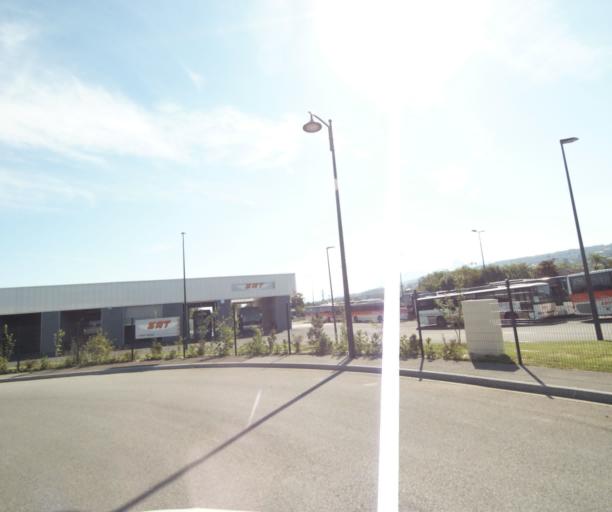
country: FR
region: Rhone-Alpes
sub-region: Departement de la Haute-Savoie
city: Thonon-les-Bains
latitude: 46.3874
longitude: 6.5035
